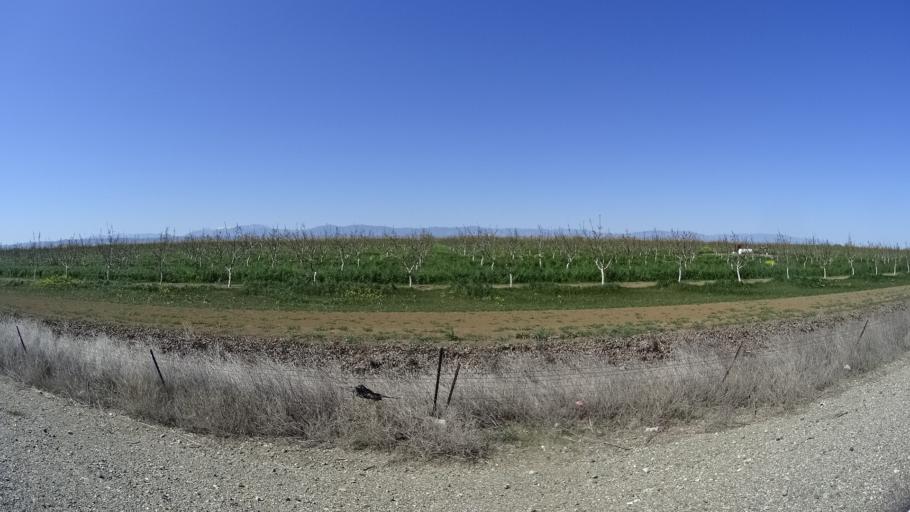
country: US
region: California
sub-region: Glenn County
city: Willows
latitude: 39.5842
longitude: -122.2497
